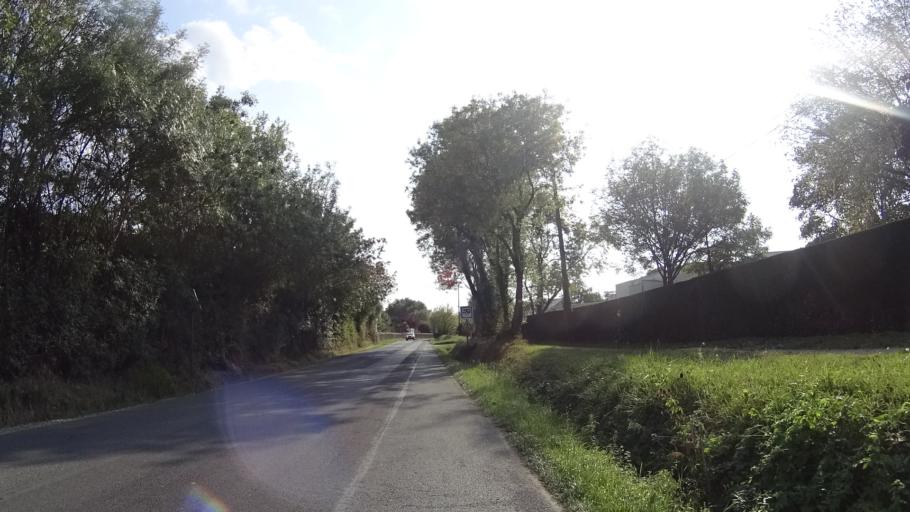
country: FR
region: Pays de la Loire
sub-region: Departement de Maine-et-Loire
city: Bouchemaine
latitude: 47.4190
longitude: -0.6118
